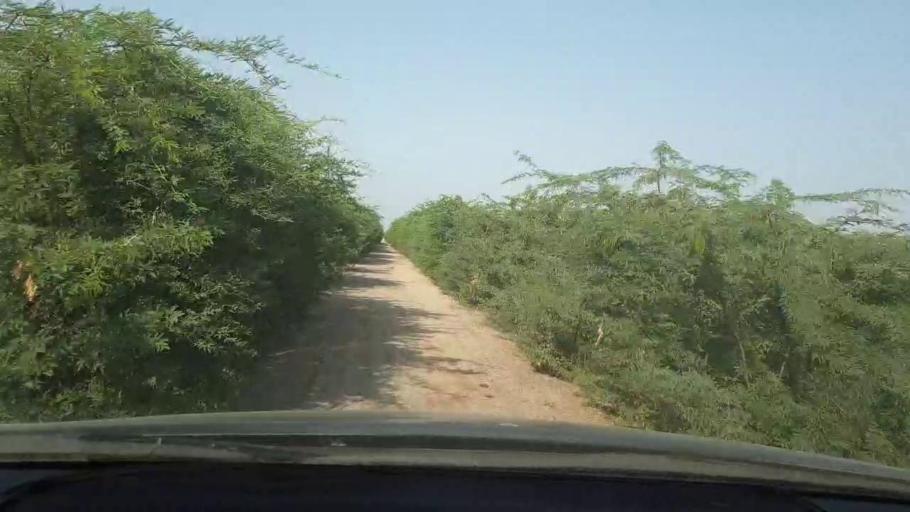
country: PK
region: Sindh
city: Naukot
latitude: 24.7932
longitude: 69.3000
